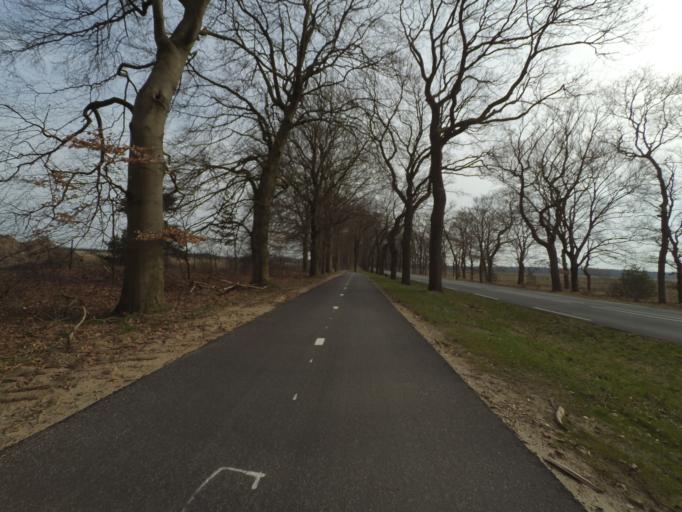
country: NL
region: Gelderland
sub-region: Gemeente Renkum
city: Wolfheze
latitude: 52.0419
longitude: 5.8106
